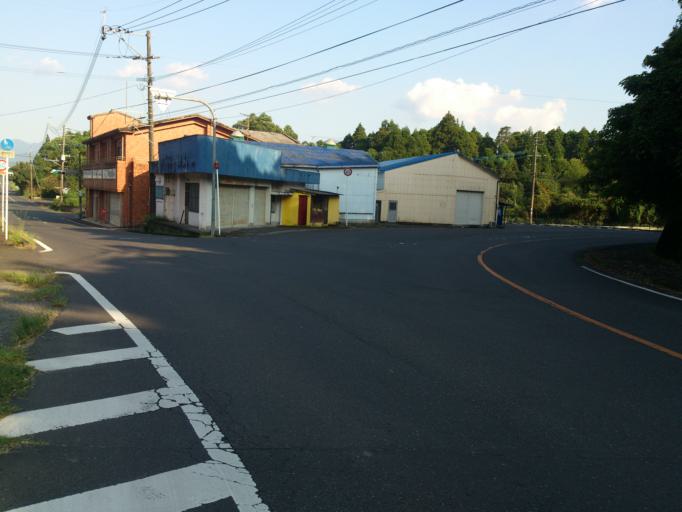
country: JP
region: Kagoshima
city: Kanoya
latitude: 31.3443
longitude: 130.8984
